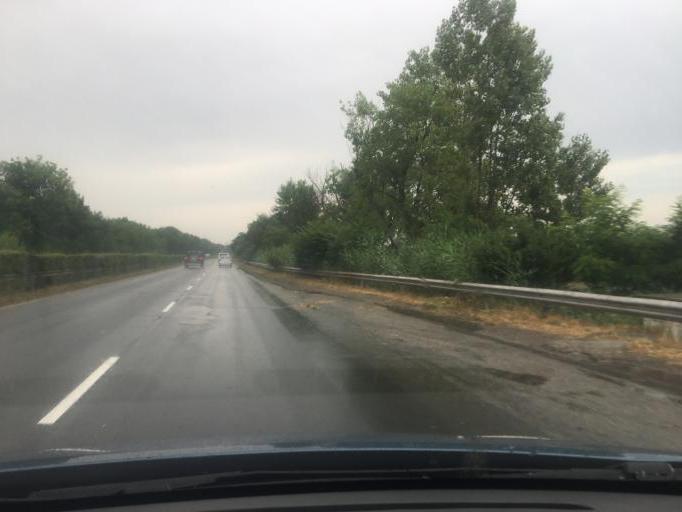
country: BG
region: Burgas
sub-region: Obshtina Burgas
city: Burgas
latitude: 42.5384
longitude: 27.4720
